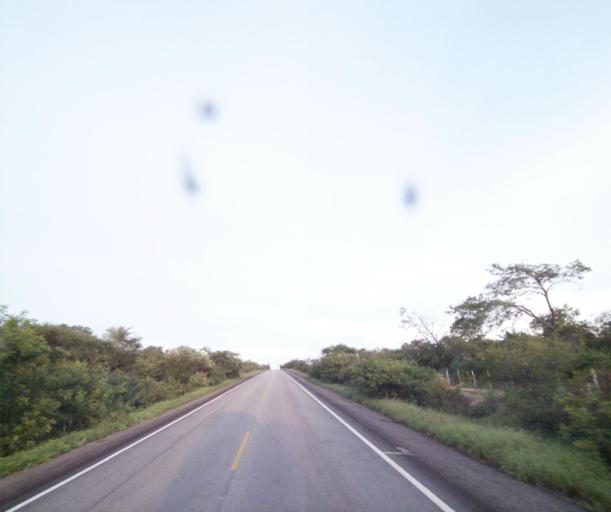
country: BR
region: Bahia
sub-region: Brumado
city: Brumado
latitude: -14.2596
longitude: -41.7896
